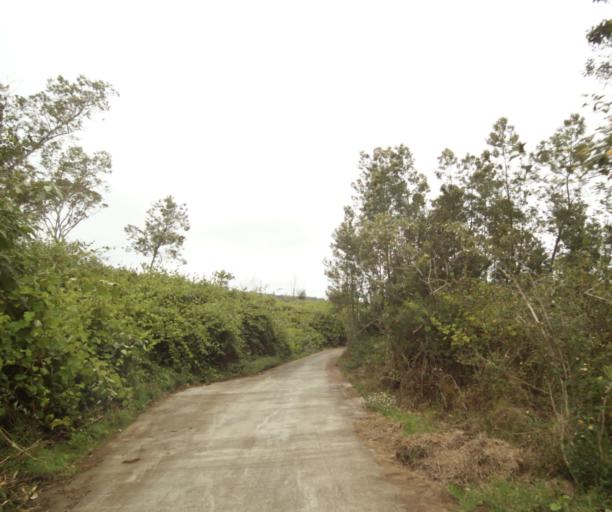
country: RE
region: Reunion
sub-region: Reunion
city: Saint-Paul
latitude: -21.0171
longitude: 55.3539
